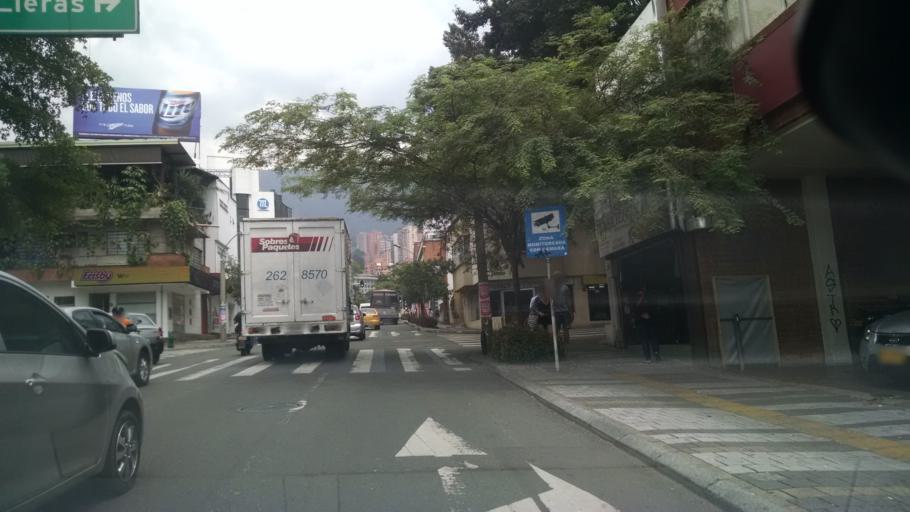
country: CO
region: Antioquia
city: Itagui
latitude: 6.2101
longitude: -75.5690
